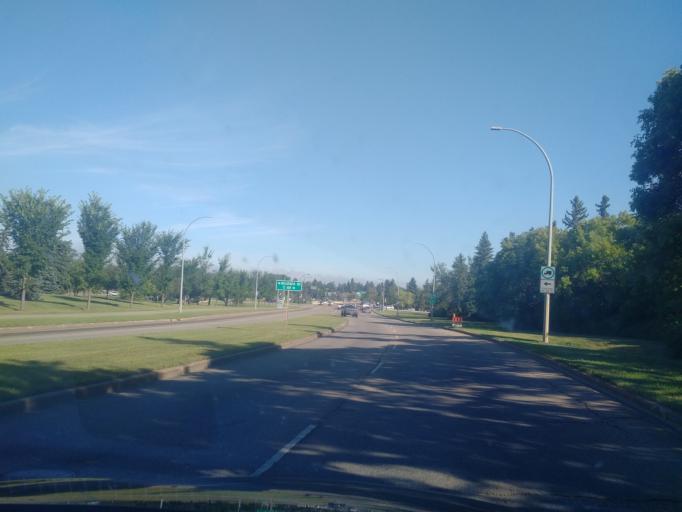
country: CA
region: Alberta
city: Edmonton
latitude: 53.5063
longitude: -113.5229
